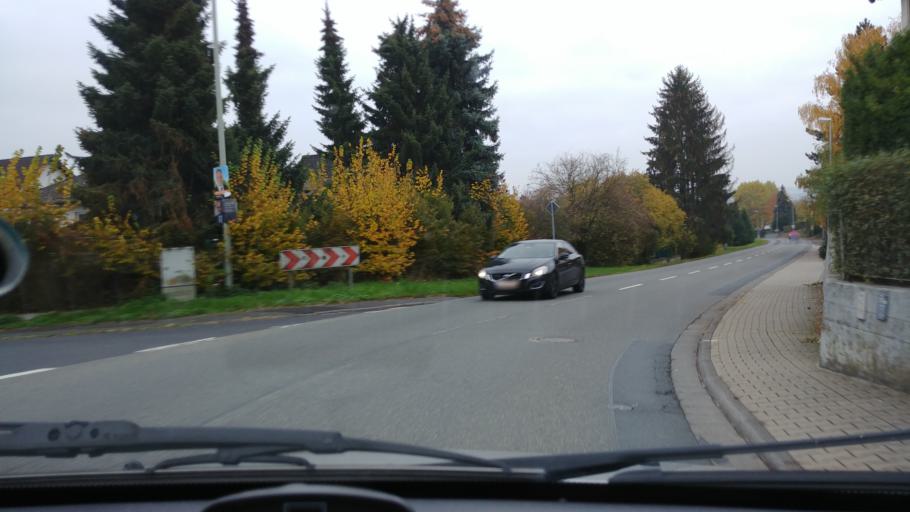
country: DE
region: Hesse
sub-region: Regierungsbezirk Giessen
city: Dehrn
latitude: 50.4257
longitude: 8.0962
